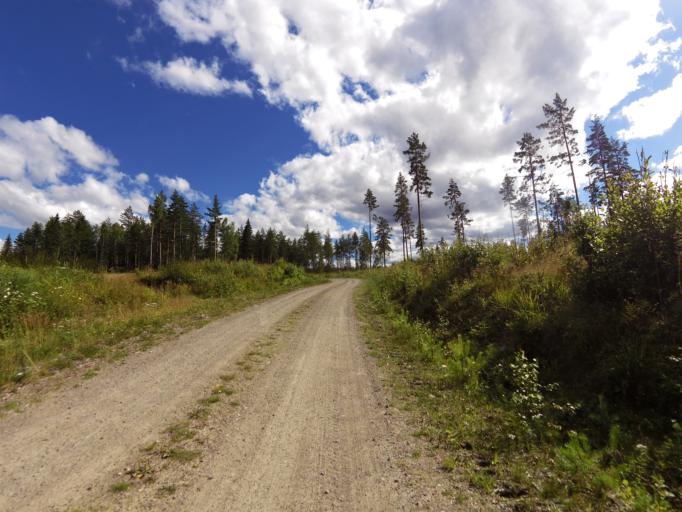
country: SE
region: Gaevleborg
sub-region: Hofors Kommun
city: Hofors
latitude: 60.5253
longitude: 16.2343
